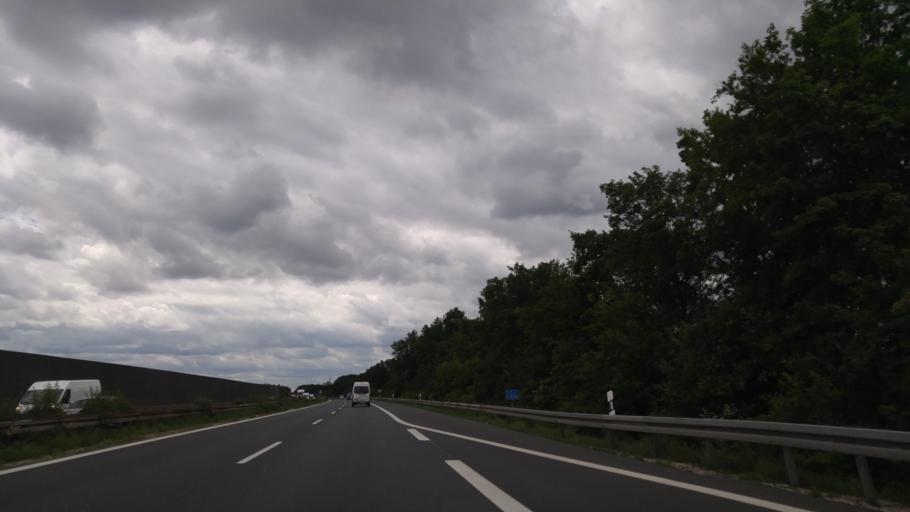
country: DE
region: Bavaria
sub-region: Regierungsbezirk Mittelfranken
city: Furth
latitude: 49.5143
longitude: 10.9923
